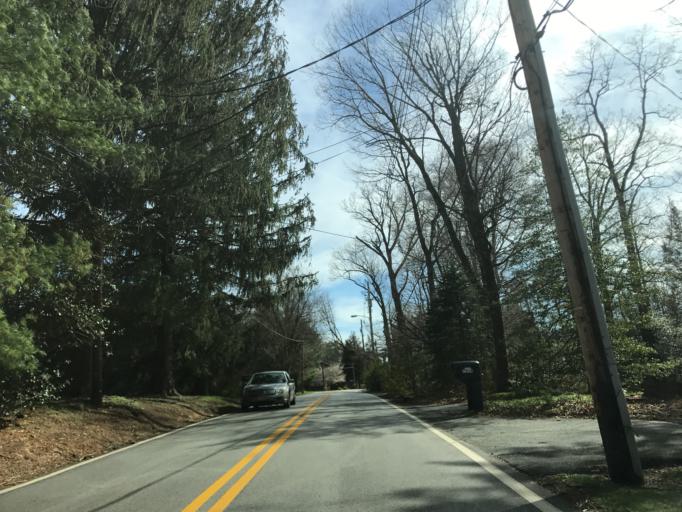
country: US
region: Maryland
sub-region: Baltimore County
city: Hampton
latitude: 39.4277
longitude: -76.5596
